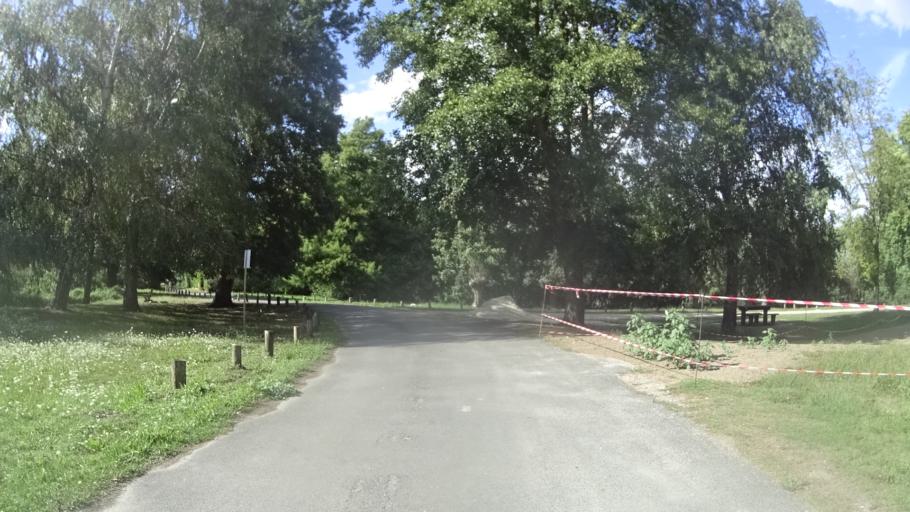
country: FR
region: Ile-de-France
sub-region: Departement de l'Essonne
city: Vert-le-Petit
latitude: 48.5532
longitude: 2.3748
